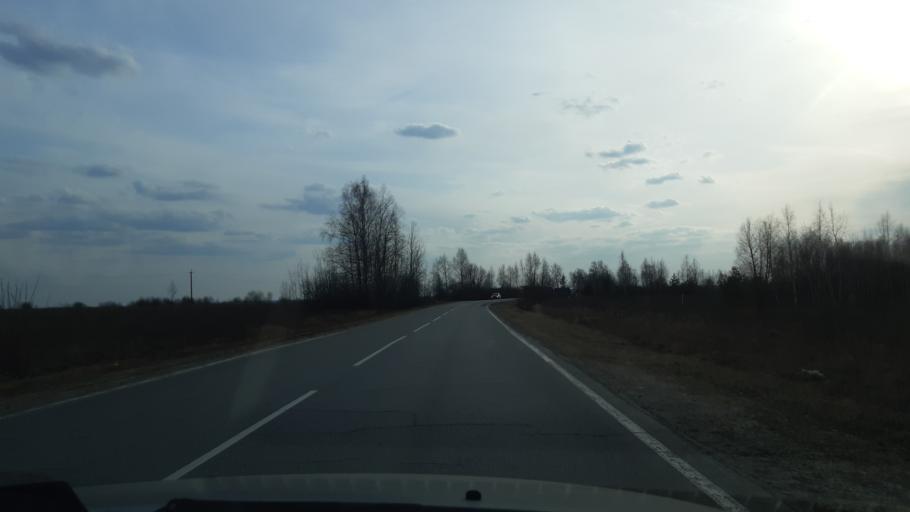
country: RU
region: Vladimir
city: Luknovo
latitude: 56.1915
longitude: 42.0274
